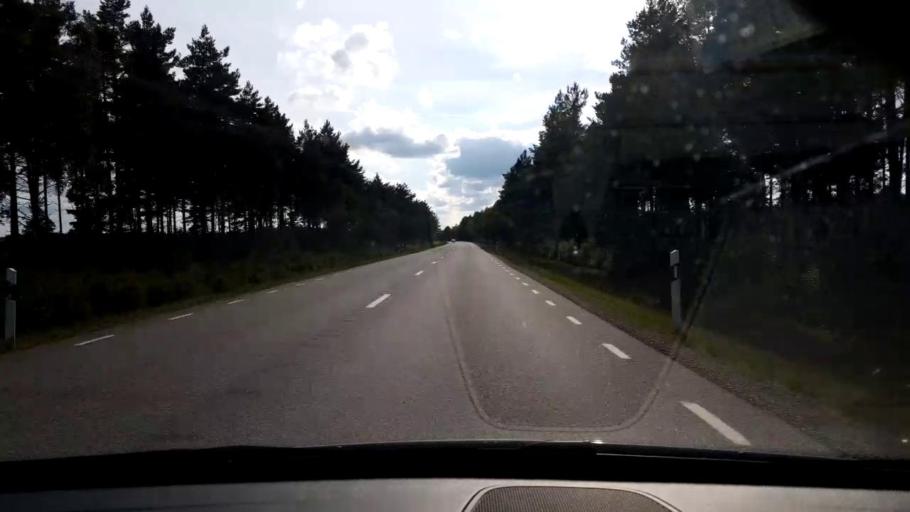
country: SE
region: Joenkoeping
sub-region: Savsjo Kommun
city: Vrigstad
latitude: 57.2876
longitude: 14.2812
